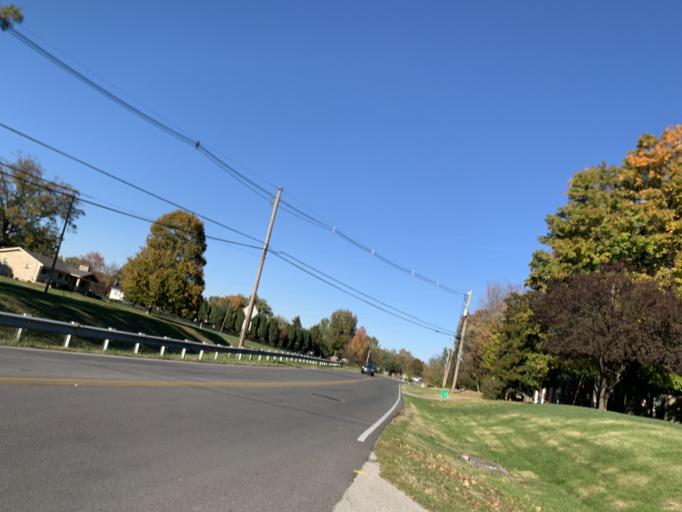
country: US
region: Kentucky
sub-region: Jefferson County
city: Saint Dennis
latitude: 38.1652
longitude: -85.8426
